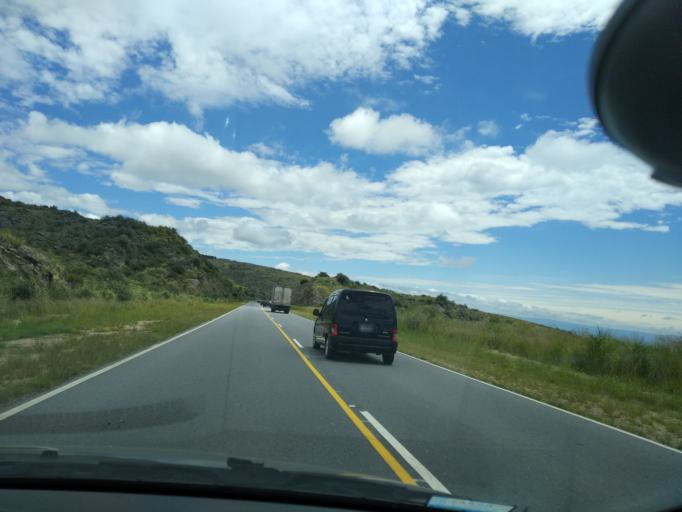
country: AR
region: Cordoba
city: Cuesta Blanca
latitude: -31.6354
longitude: -64.6765
